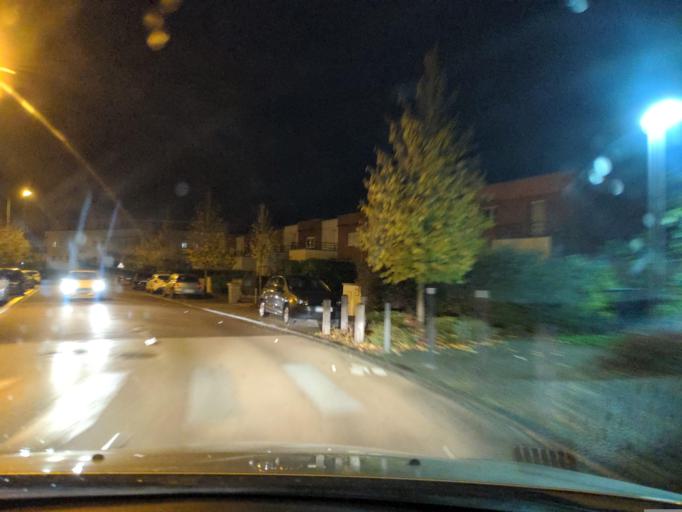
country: FR
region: Bourgogne
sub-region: Departement de la Cote-d'Or
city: Saint-Apollinaire
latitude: 47.3270
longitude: 5.0817
